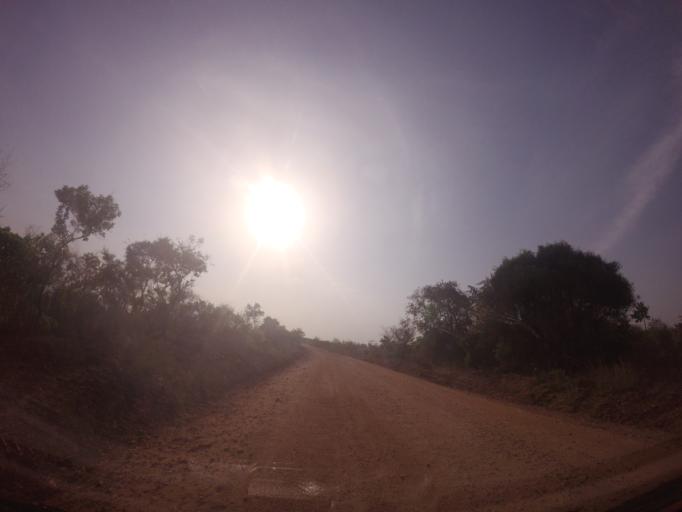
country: UG
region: Northern Region
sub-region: Maracha District
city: Maracha
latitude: 3.1130
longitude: 31.1455
